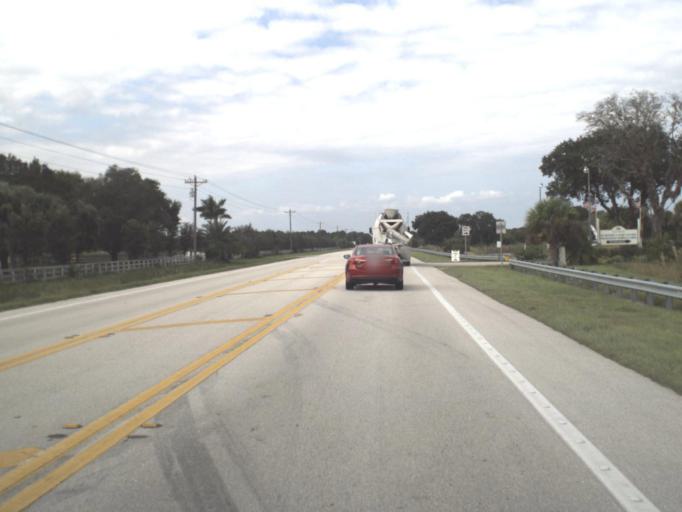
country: US
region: Florida
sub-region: Glades County
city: Moore Haven
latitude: 26.7684
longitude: -81.2266
